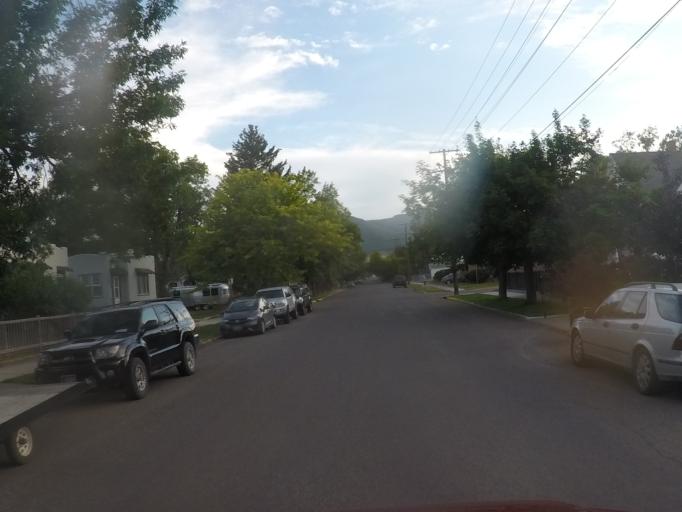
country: US
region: Montana
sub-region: Park County
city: Livingston
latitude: 45.6556
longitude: -110.5619
